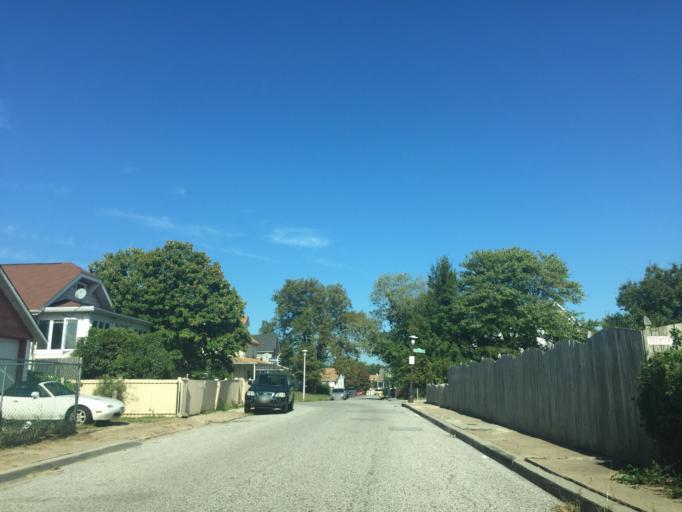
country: US
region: Maryland
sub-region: Baltimore County
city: Rosedale
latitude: 39.3320
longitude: -76.5581
